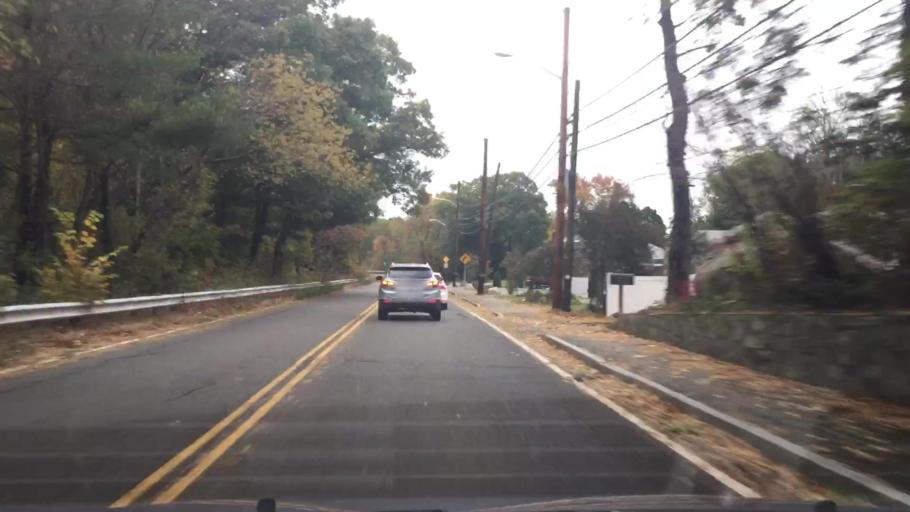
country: US
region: Massachusetts
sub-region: Essex County
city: Saugus
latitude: 42.5017
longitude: -71.0227
